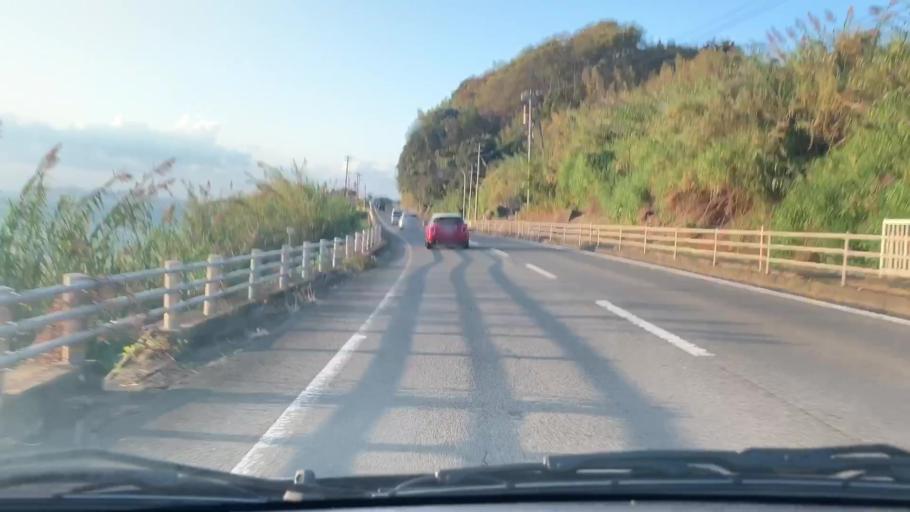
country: JP
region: Nagasaki
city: Omura
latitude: 32.9967
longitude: 129.9480
